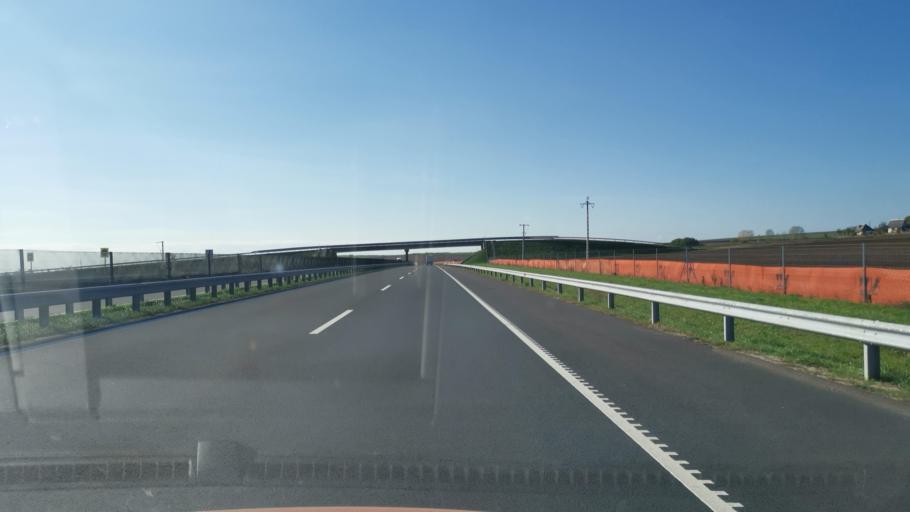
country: HU
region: Borsod-Abauj-Zemplen
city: Halmaj
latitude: 48.2893
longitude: 21.0247
